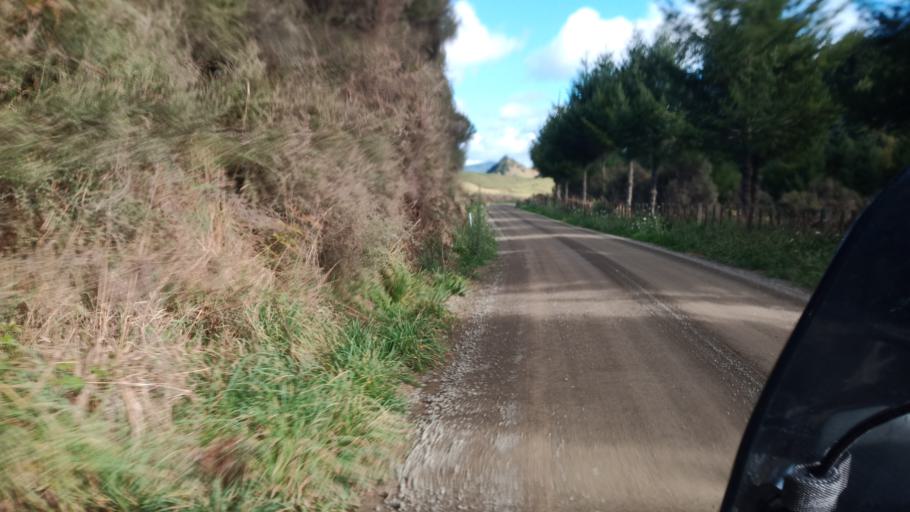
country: NZ
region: Bay of Plenty
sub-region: Opotiki District
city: Opotiki
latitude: -38.4576
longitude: 177.4089
